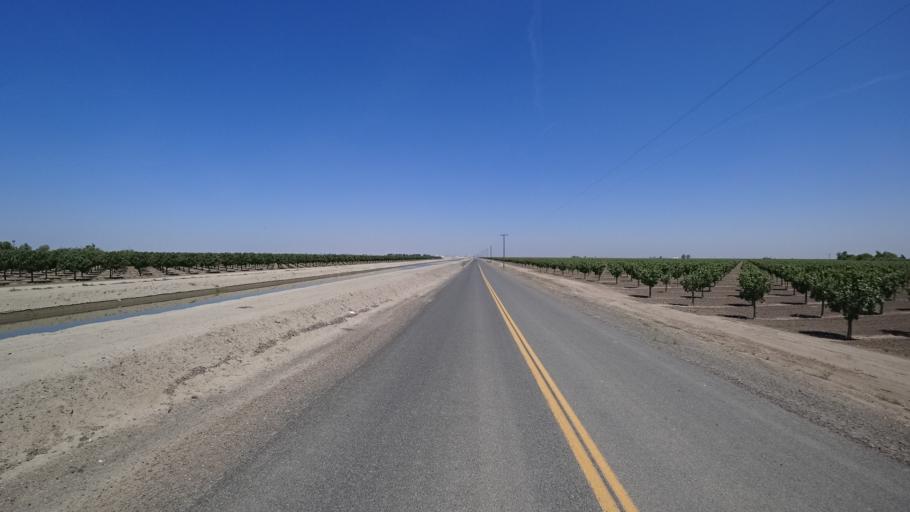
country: US
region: California
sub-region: Kings County
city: Corcoran
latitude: 36.0365
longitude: -119.5362
